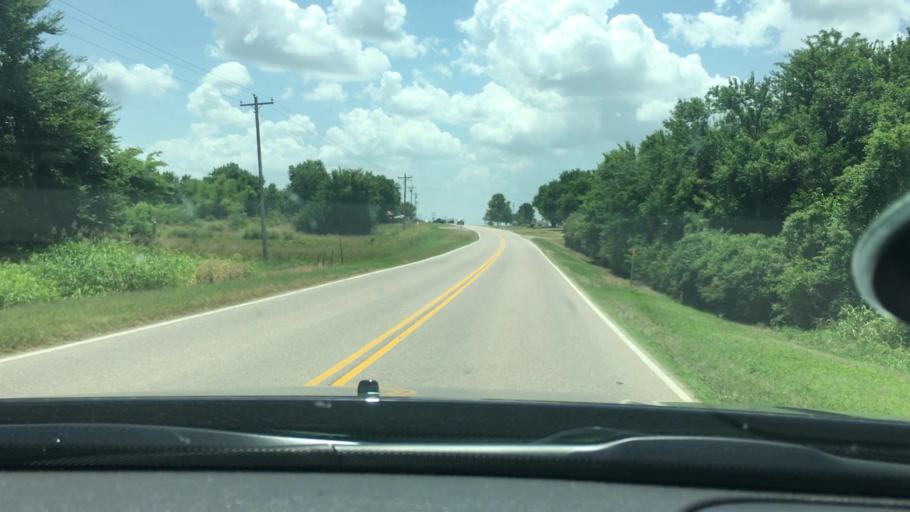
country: US
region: Oklahoma
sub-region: Johnston County
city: Tishomingo
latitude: 34.4468
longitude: -96.6363
